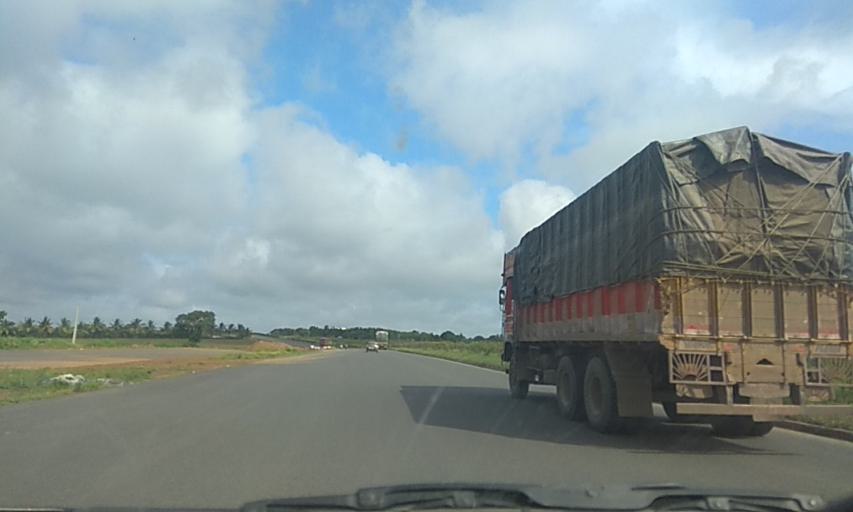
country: IN
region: Karnataka
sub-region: Haveri
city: Shiggaon
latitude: 15.0032
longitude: 75.2050
